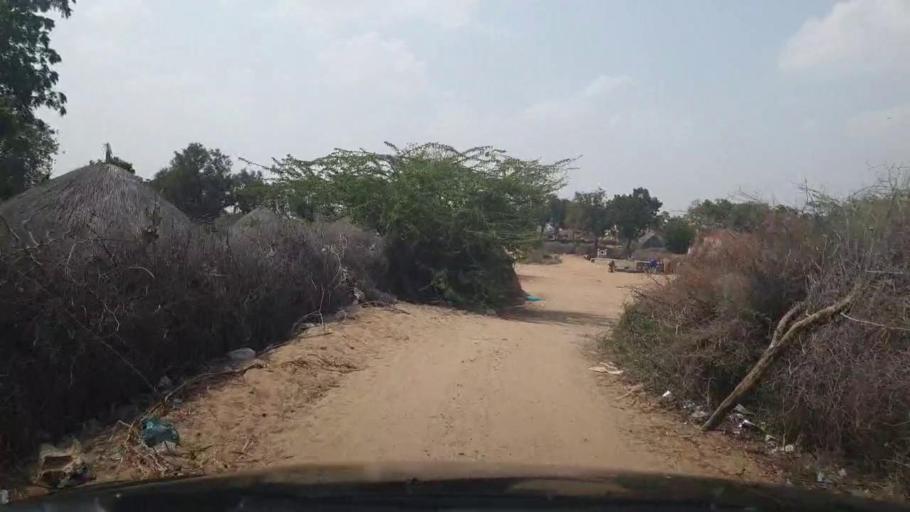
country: PK
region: Sindh
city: Islamkot
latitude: 24.9929
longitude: 70.4918
